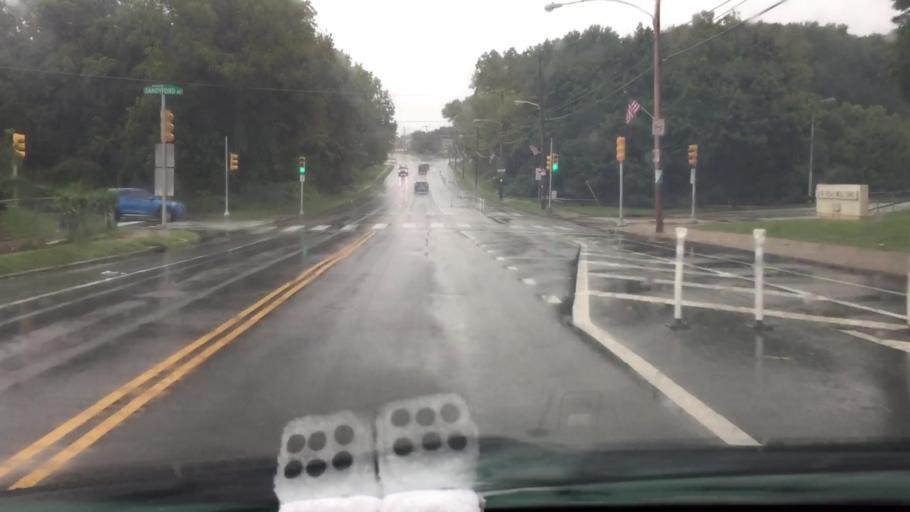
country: US
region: New Jersey
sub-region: Burlington County
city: Palmyra
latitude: 40.0461
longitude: -75.0453
